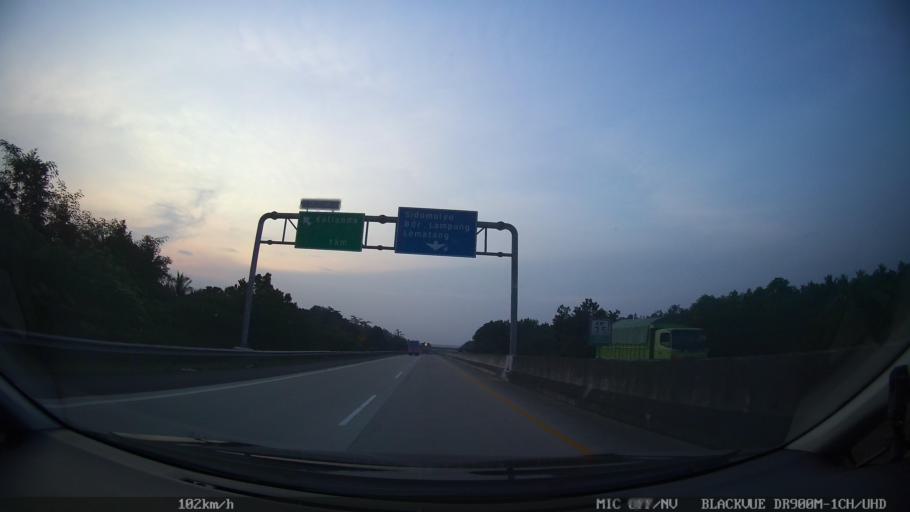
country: ID
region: Lampung
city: Kalianda
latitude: -5.6997
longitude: 105.6311
